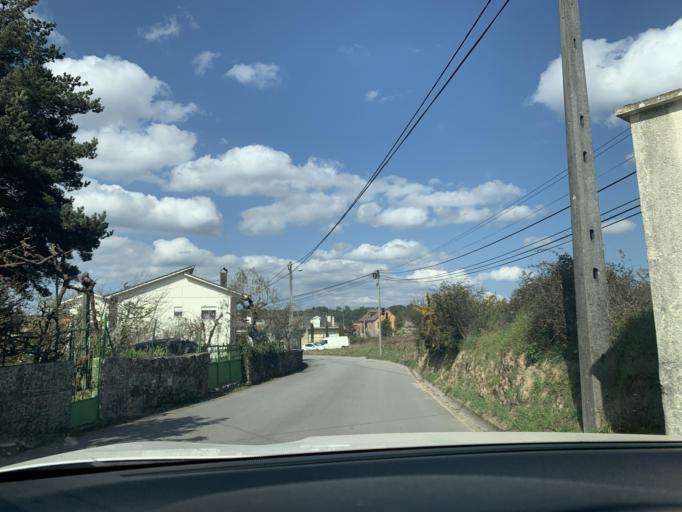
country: PT
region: Viseu
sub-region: Viseu
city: Rio de Loba
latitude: 40.6767
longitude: -7.8830
